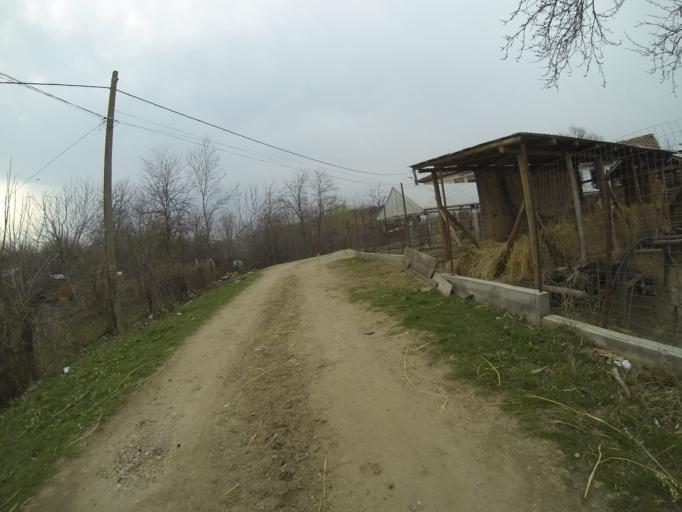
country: RO
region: Dolj
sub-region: Comuna Bucovat
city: Bucovat
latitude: 44.2677
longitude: 23.7207
